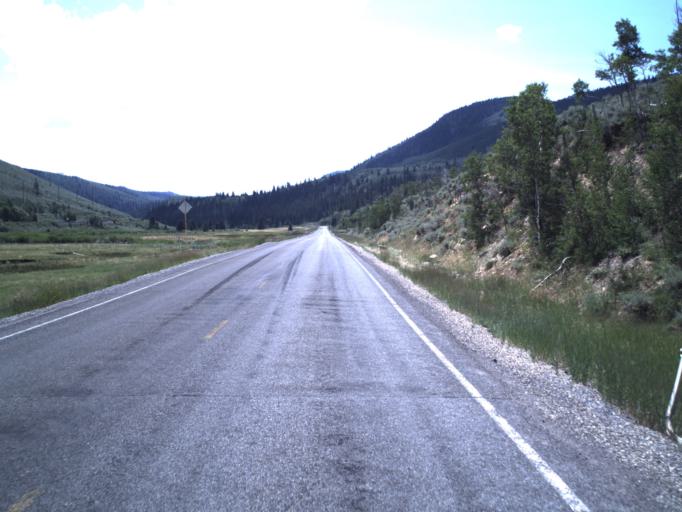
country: US
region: Utah
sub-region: Sanpete County
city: Fairview
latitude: 39.7178
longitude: -111.1633
